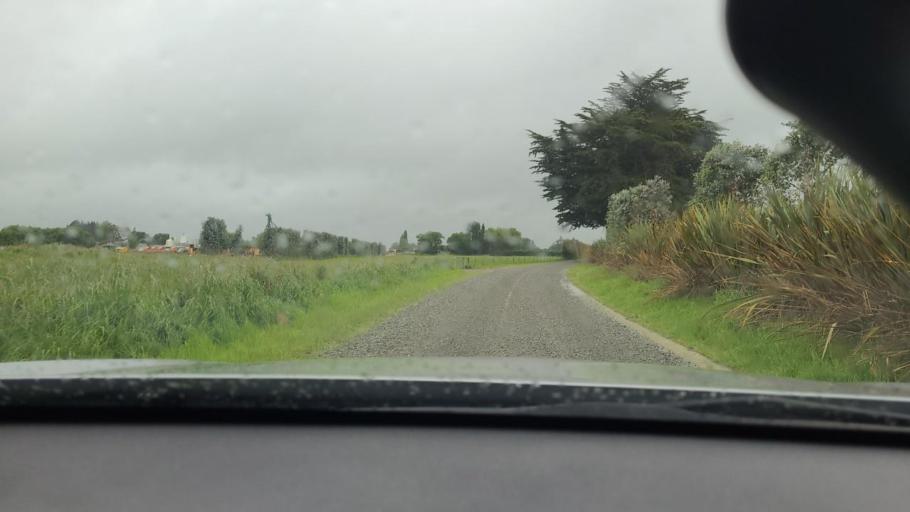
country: NZ
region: Southland
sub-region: Southland District
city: Winton
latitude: -46.1571
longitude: 168.3349
